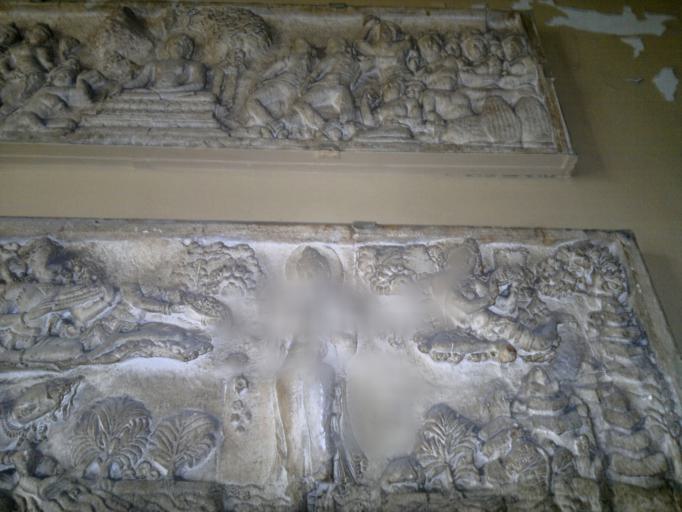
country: RU
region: St.-Petersburg
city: Saint Petersburg
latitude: 59.9415
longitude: 30.3038
